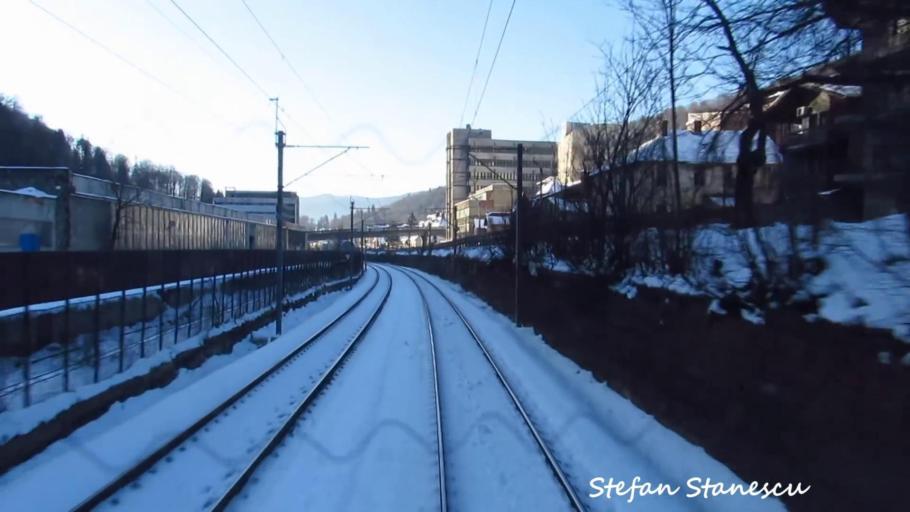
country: RO
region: Prahova
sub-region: Oras Sinaia
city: Sinaia
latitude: 45.3431
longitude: 25.5509
